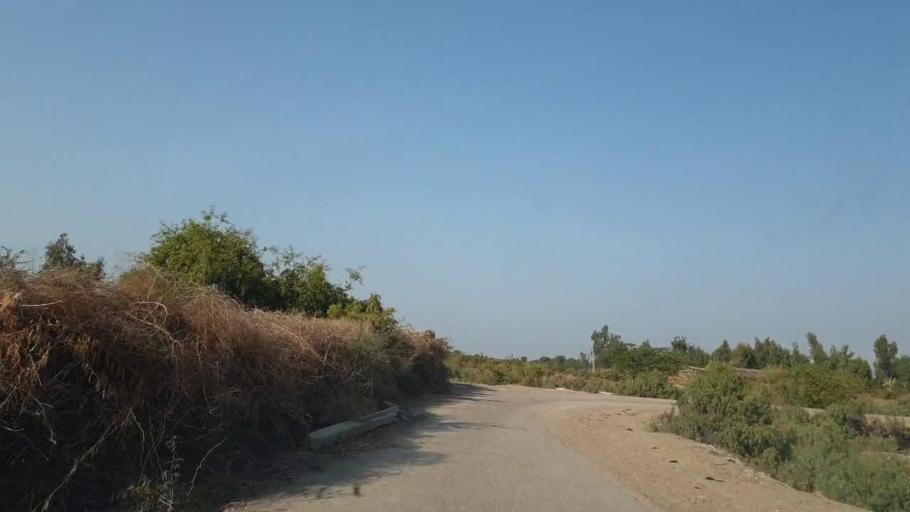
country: PK
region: Sindh
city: Tando Mittha Khan
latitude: 25.7543
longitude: 69.2006
